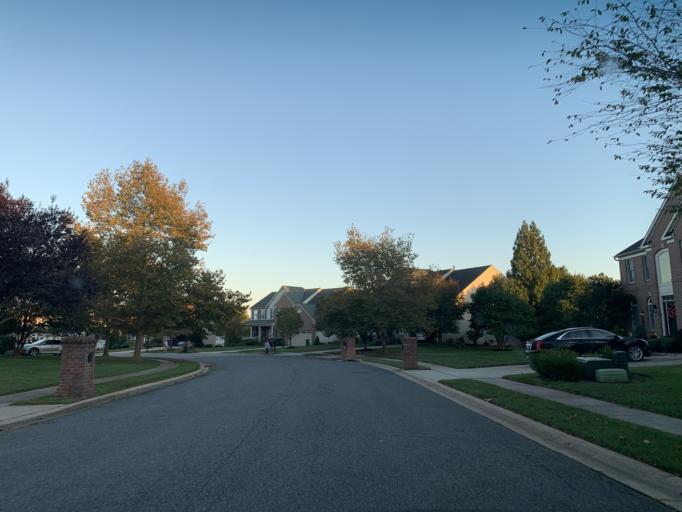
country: US
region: Maryland
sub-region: Harford County
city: Bel Air South
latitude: 39.5280
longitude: -76.3009
